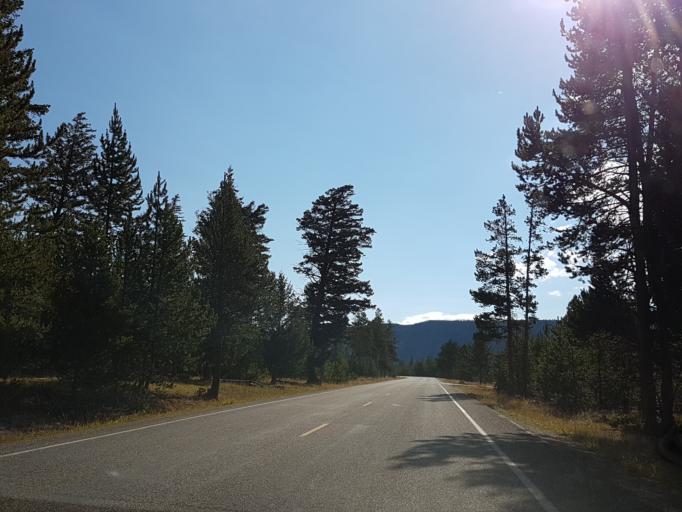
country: US
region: Montana
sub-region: Gallatin County
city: West Yellowstone
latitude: 44.6472
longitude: -110.9309
